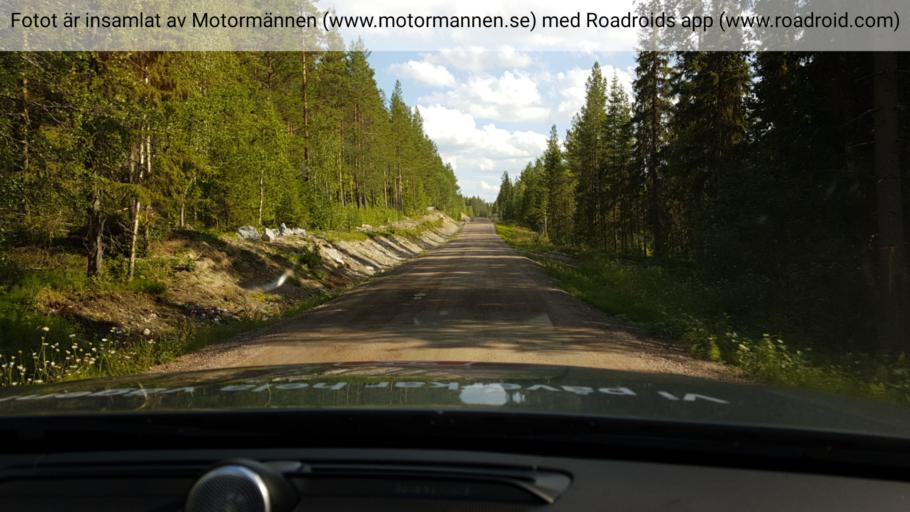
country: SE
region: Vaesterbotten
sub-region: Dorotea Kommun
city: Dorotea
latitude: 63.9662
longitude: 16.0701
